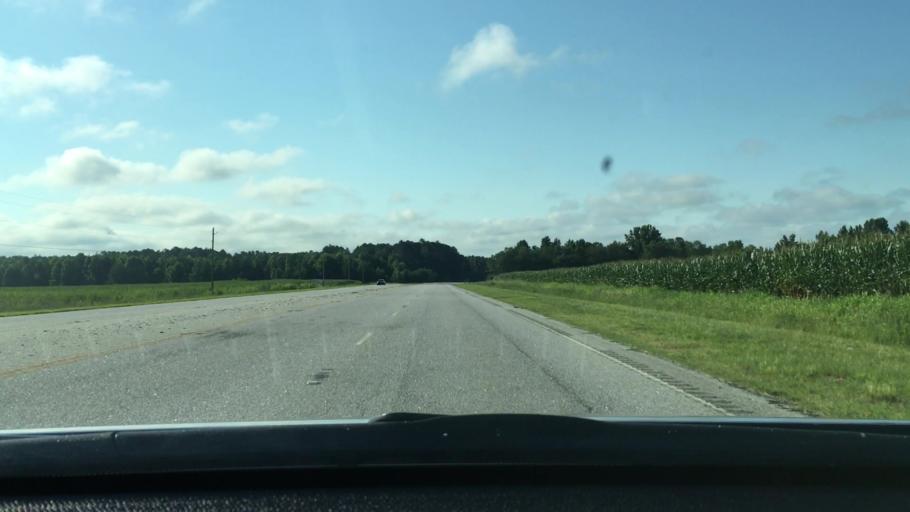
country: US
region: South Carolina
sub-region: Clarendon County
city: Manning
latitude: 33.7785
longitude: -80.2435
